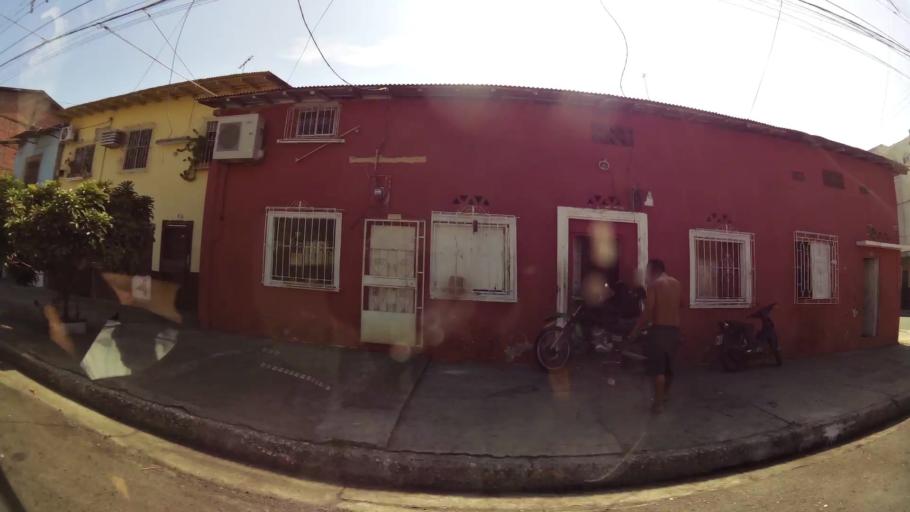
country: EC
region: Guayas
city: Guayaquil
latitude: -2.2152
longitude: -79.8980
